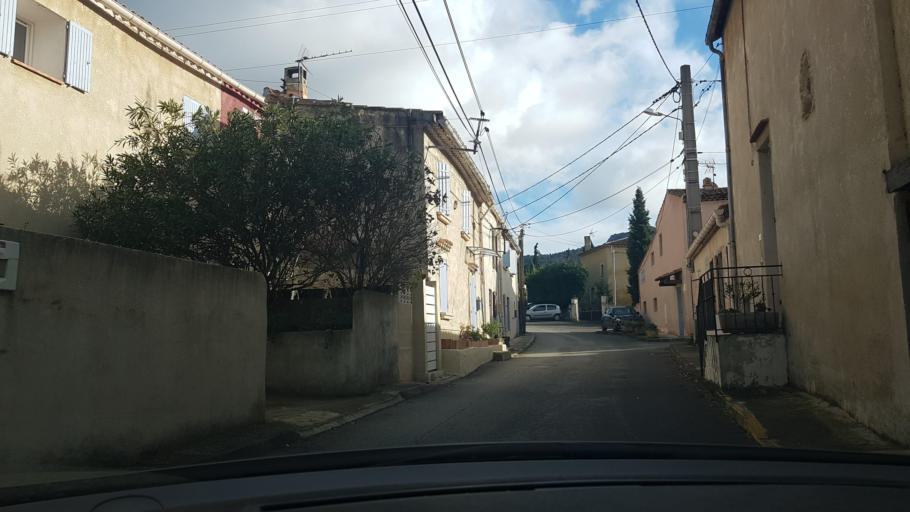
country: FR
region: Provence-Alpes-Cote d'Azur
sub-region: Departement des Bouches-du-Rhone
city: Simiane-Collongue
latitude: 43.4198
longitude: 5.4595
